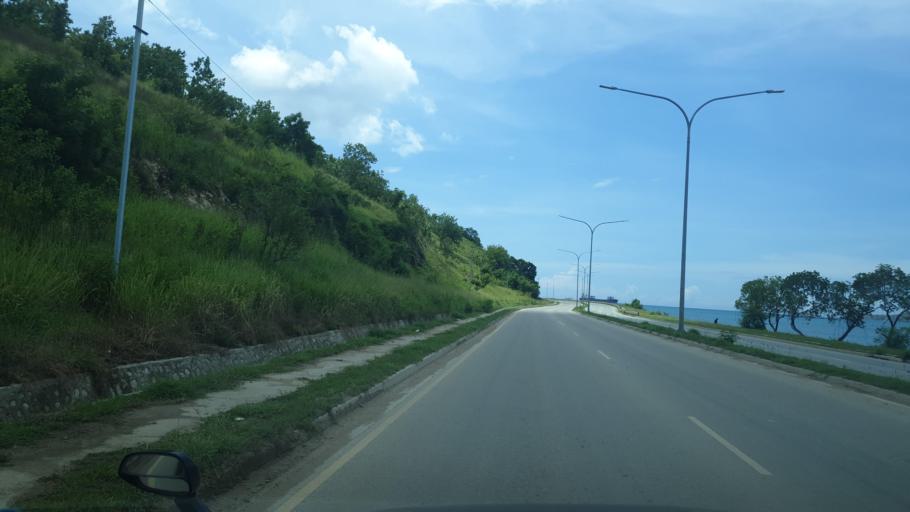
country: PG
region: National Capital
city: Port Moresby
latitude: -9.4402
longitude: 147.1408
